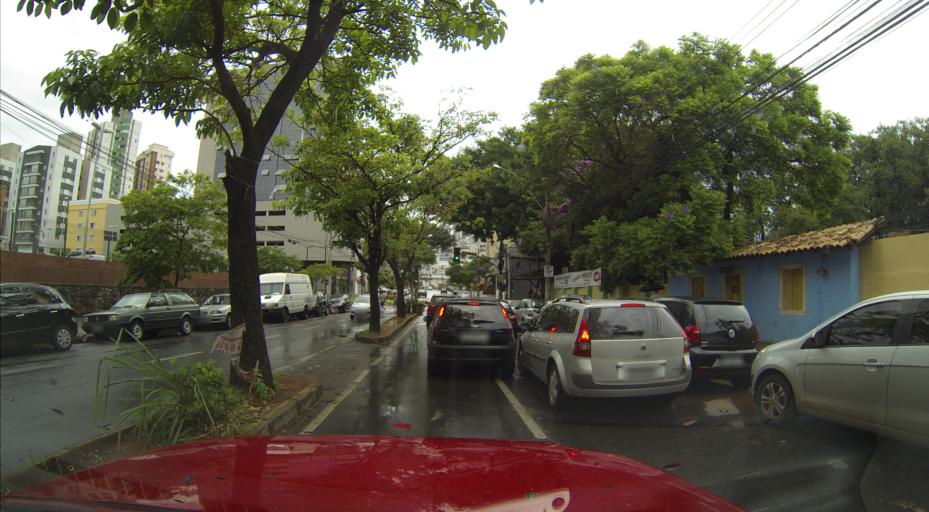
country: BR
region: Minas Gerais
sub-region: Belo Horizonte
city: Belo Horizonte
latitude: -19.9676
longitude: -43.9628
